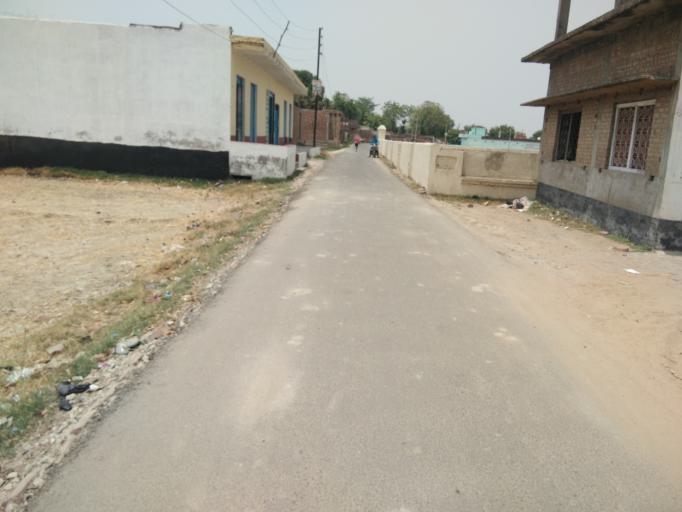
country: IN
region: Uttar Pradesh
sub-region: Ghazipur
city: Zamania
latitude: 25.4399
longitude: 83.6845
